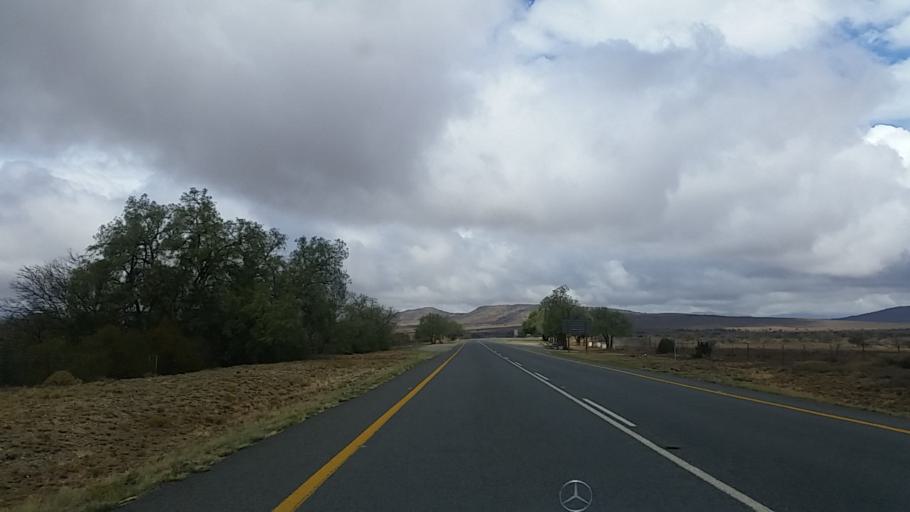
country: ZA
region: Eastern Cape
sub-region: Cacadu District Municipality
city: Graaff-Reinet
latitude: -32.0681
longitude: 24.6059
